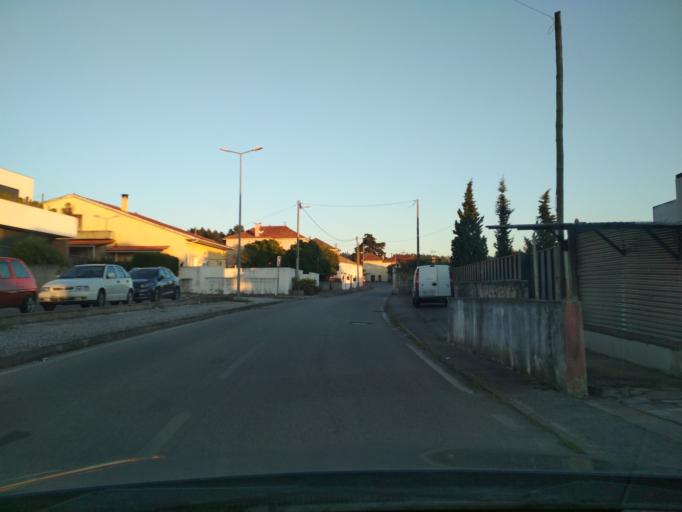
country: PT
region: Coimbra
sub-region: Condeixa-A-Nova
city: Condeixa-a-Nova
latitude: 40.1751
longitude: -8.4836
